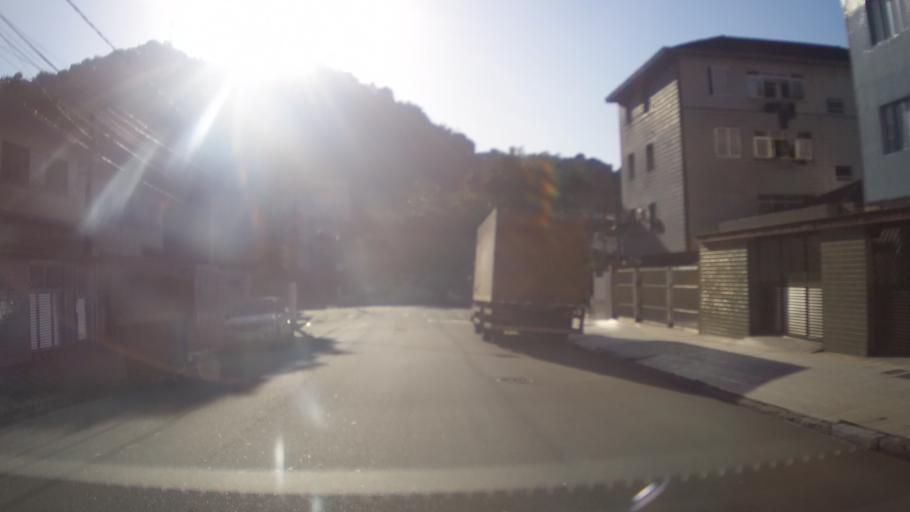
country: BR
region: Sao Paulo
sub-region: Santos
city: Santos
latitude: -23.9407
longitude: -46.3367
